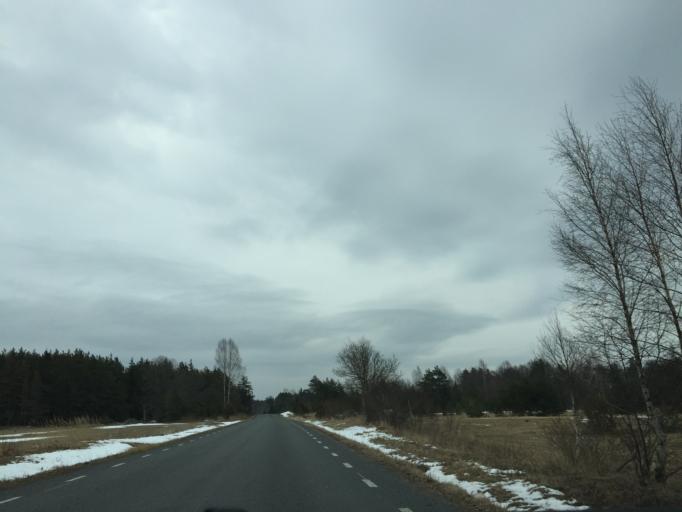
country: EE
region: Saare
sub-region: Kuressaare linn
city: Kuressaare
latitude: 58.4172
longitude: 22.1320
